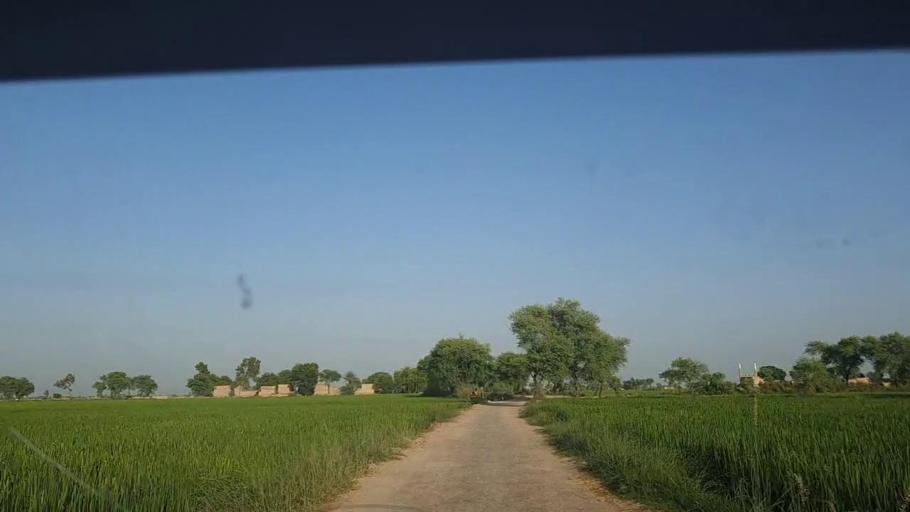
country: PK
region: Sindh
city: Thul
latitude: 28.2142
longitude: 68.8753
